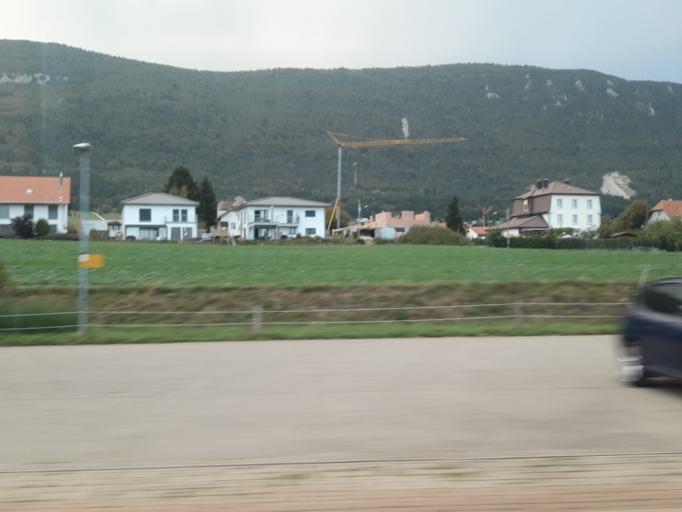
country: CH
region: Solothurn
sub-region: Bezirk Lebern
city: Selzach
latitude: 47.2186
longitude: 7.4699
